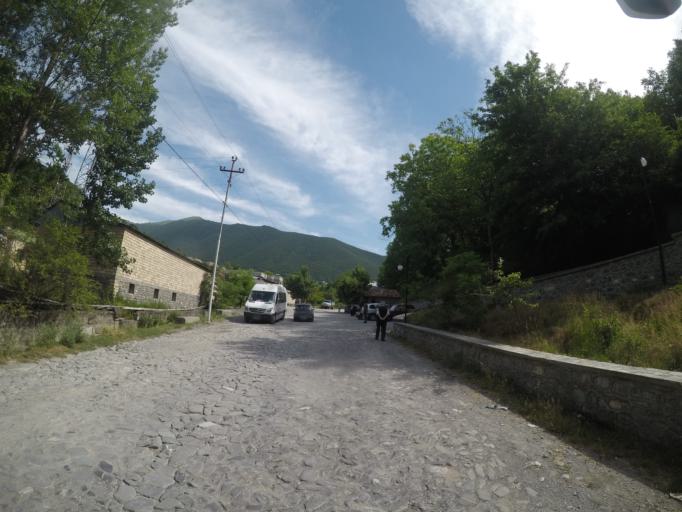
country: AZ
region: Shaki City
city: Sheki
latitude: 41.2477
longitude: 47.1890
